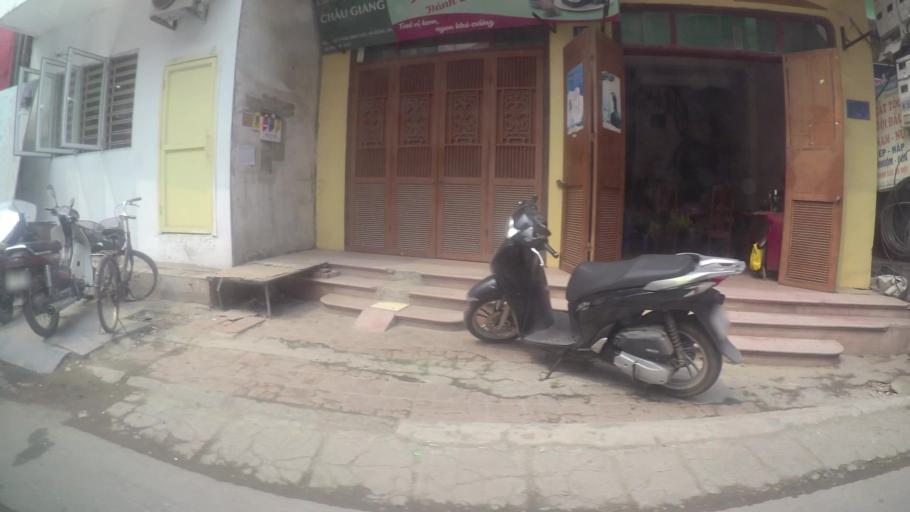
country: VN
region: Ha Noi
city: Ha Dong
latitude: 20.9646
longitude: 105.7670
